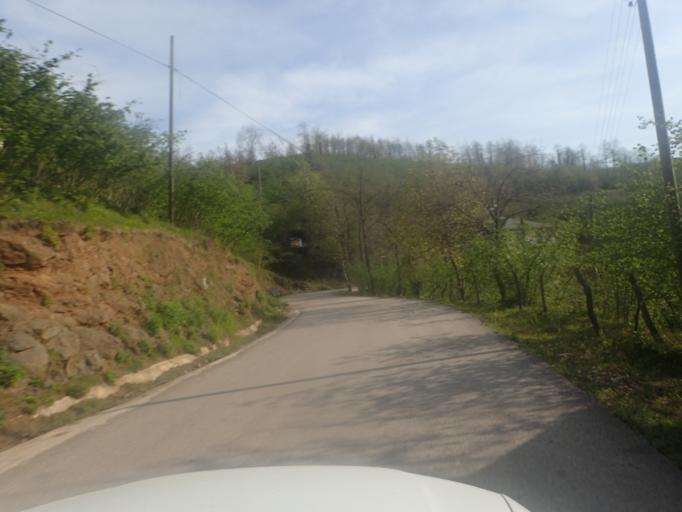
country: TR
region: Ordu
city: Catalpinar
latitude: 40.8834
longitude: 37.4861
